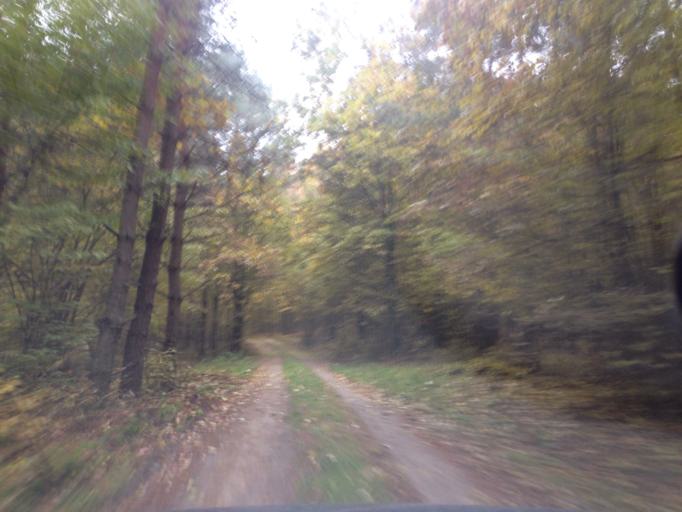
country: PL
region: Kujawsko-Pomorskie
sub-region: Powiat brodnicki
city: Gorzno
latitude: 53.2212
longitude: 19.7172
